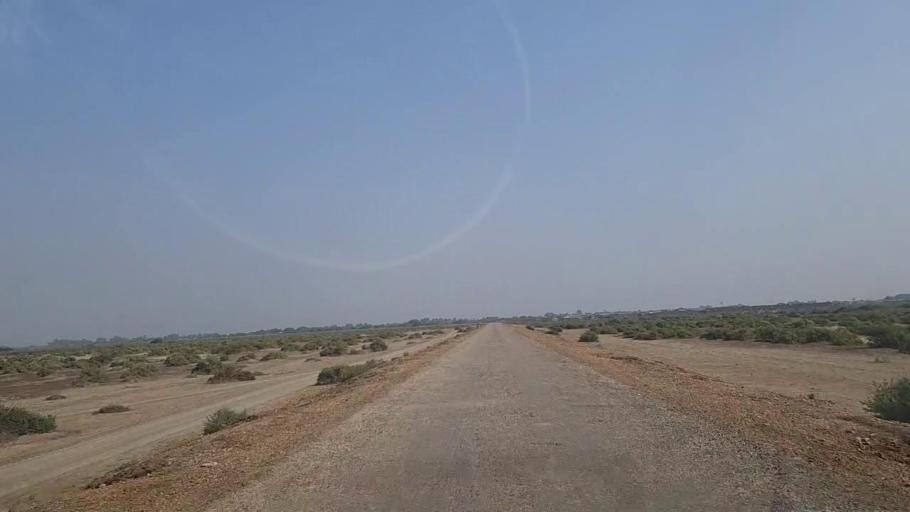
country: PK
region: Sindh
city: Keti Bandar
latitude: 24.2401
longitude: 67.6860
